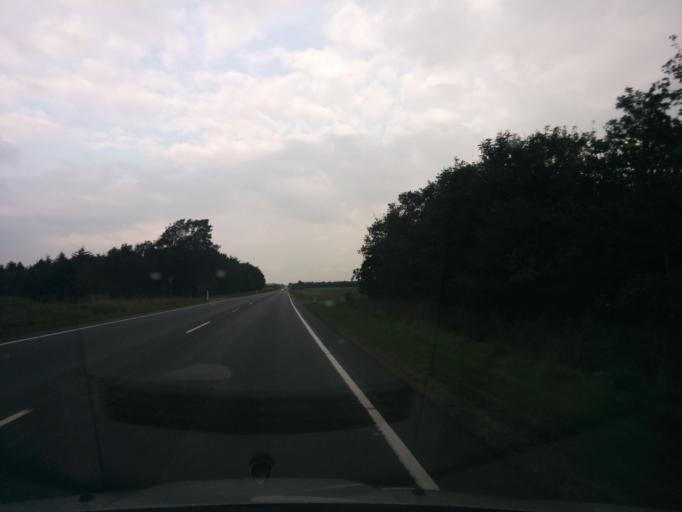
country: DK
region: South Denmark
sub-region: Esbjerg Kommune
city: Bramming
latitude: 55.5850
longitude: 8.6987
